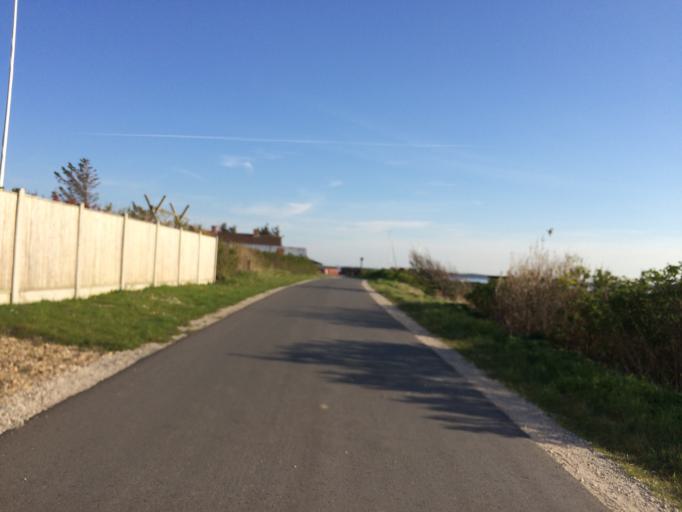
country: DK
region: Central Jutland
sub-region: Struer Kommune
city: Struer
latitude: 56.5524
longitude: 8.6164
